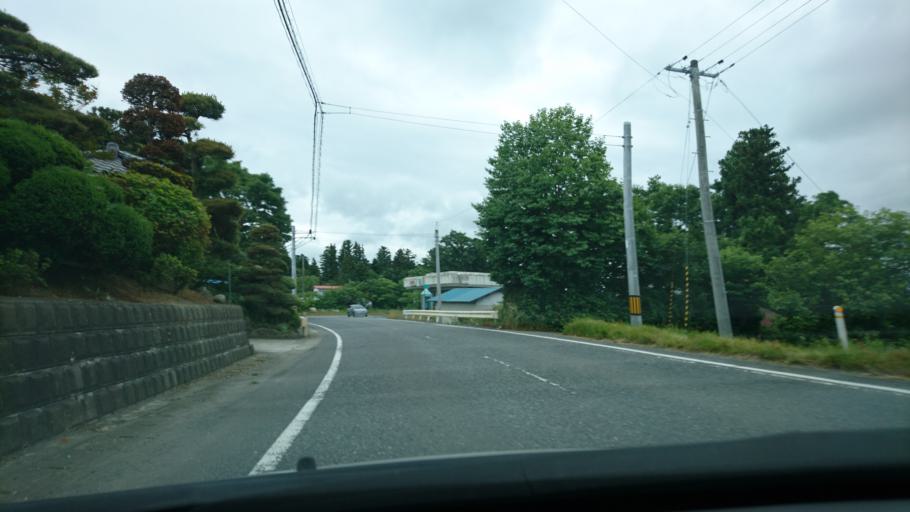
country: JP
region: Iwate
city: Ichinoseki
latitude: 38.7538
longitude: 141.2549
